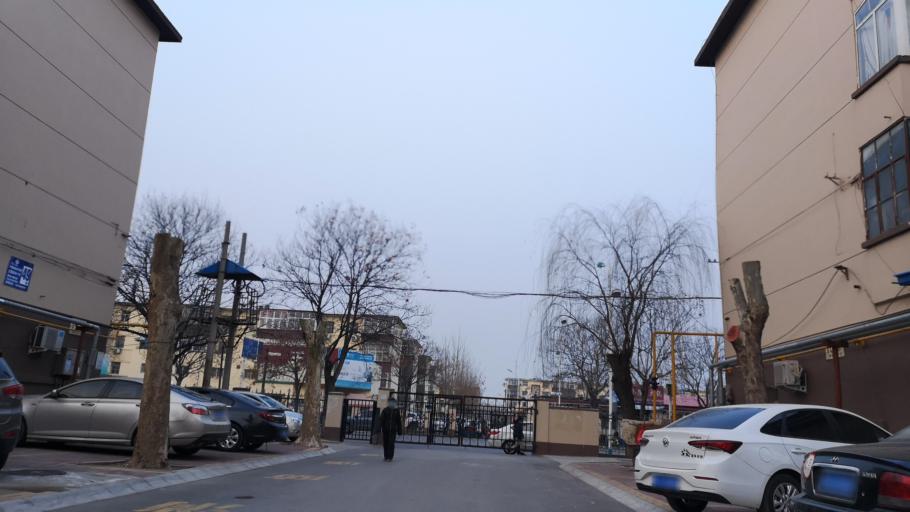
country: CN
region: Henan Sheng
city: Zhongyuanlu
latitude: 35.7843
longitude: 115.0732
